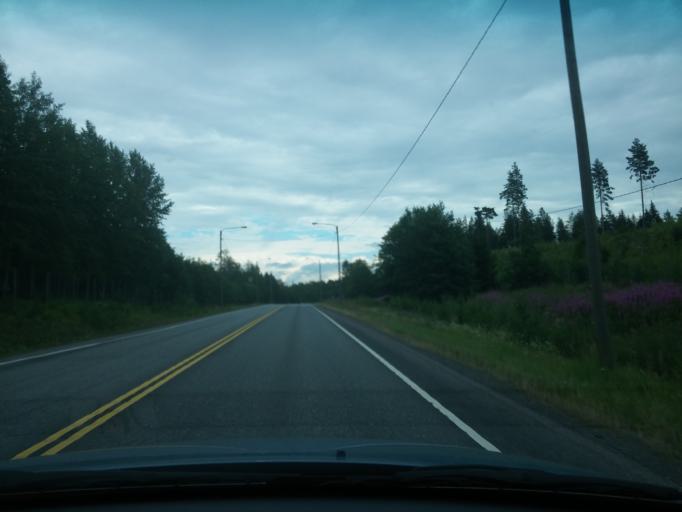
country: FI
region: Haeme
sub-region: Riihimaeki
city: Loppi
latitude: 60.7309
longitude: 24.5304
